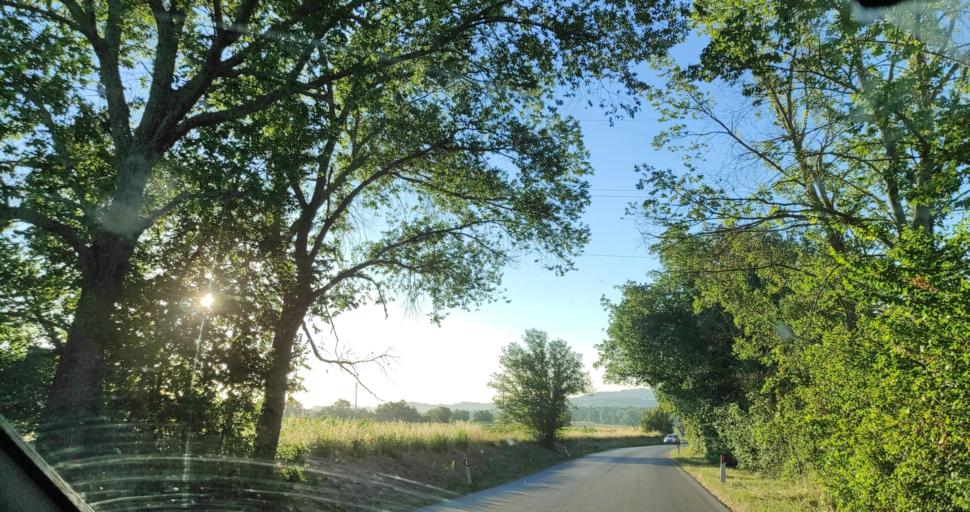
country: IT
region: The Marches
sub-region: Provincia di Macerata
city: Casette Verdini
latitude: 43.2290
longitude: 13.3997
